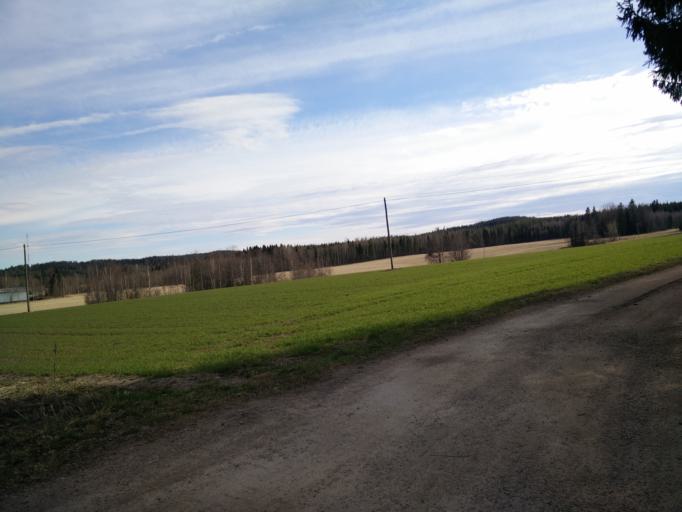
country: FI
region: Pirkanmaa
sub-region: Tampere
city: Orivesi
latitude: 61.7032
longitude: 24.3388
